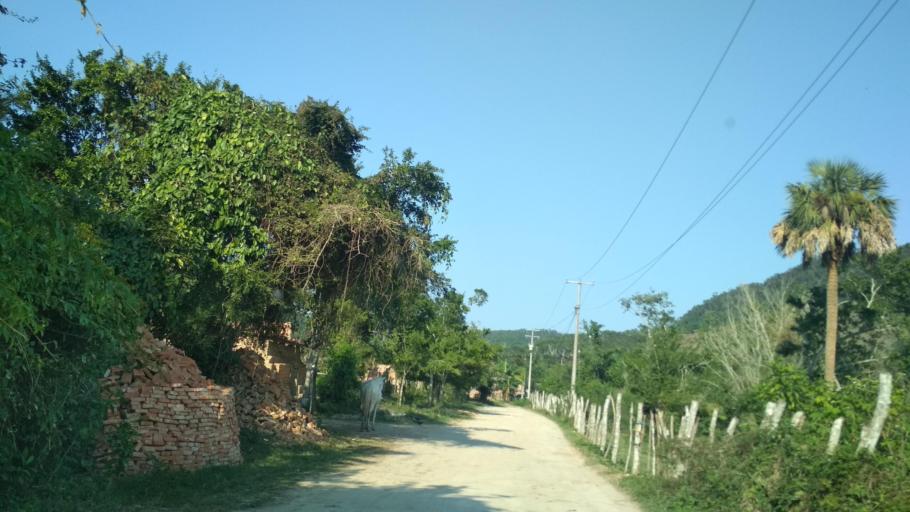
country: MM
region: Shan
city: Taunggyi
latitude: 20.4009
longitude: 97.3298
